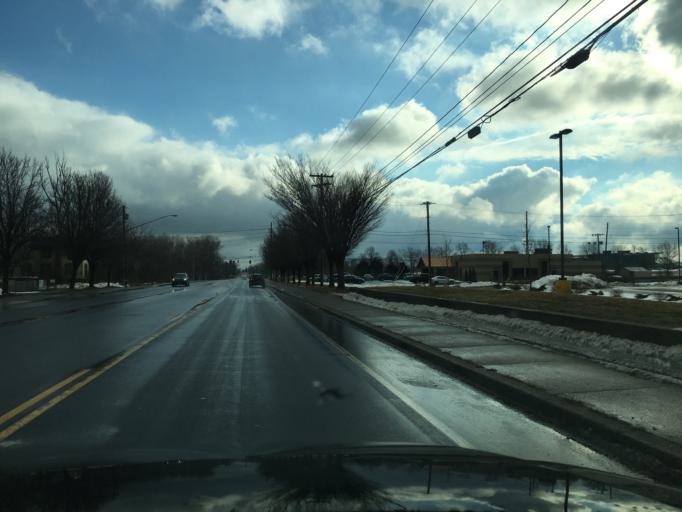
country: US
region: New York
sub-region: Ontario County
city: Victor
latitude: 42.9744
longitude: -77.3512
